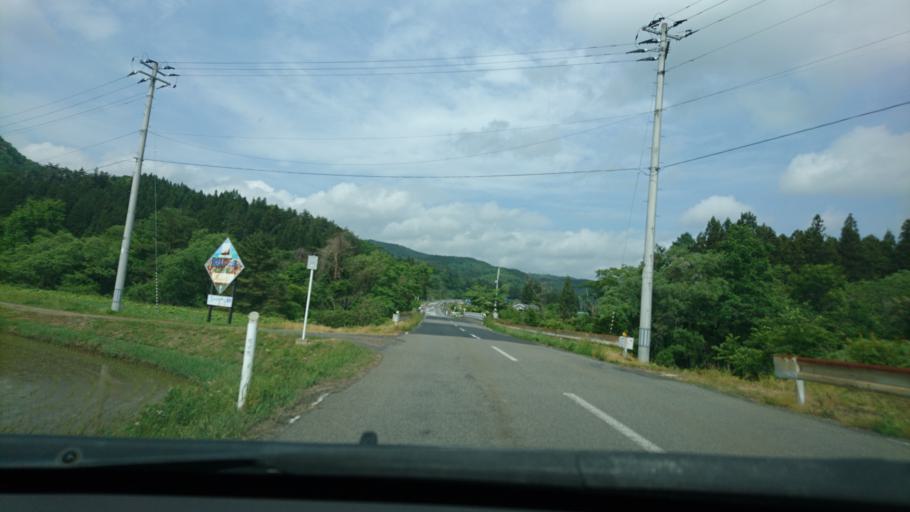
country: JP
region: Iwate
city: Ichinoseki
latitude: 38.8926
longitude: 140.9461
